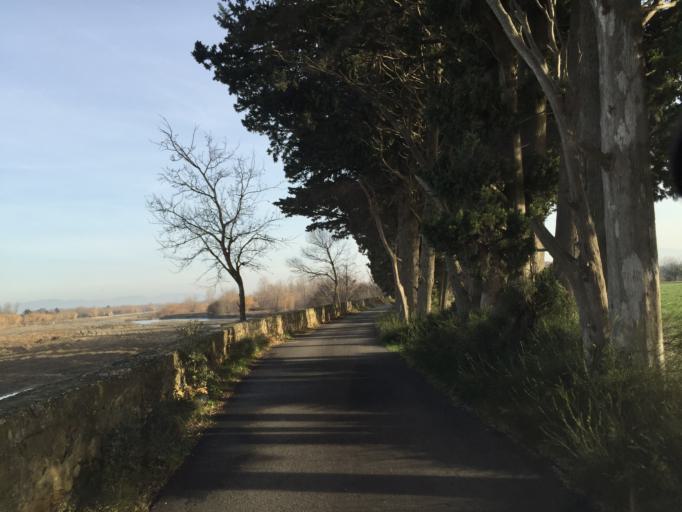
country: FR
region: Provence-Alpes-Cote d'Azur
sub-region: Departement du Vaucluse
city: Orange
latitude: 44.1620
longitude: 4.8206
